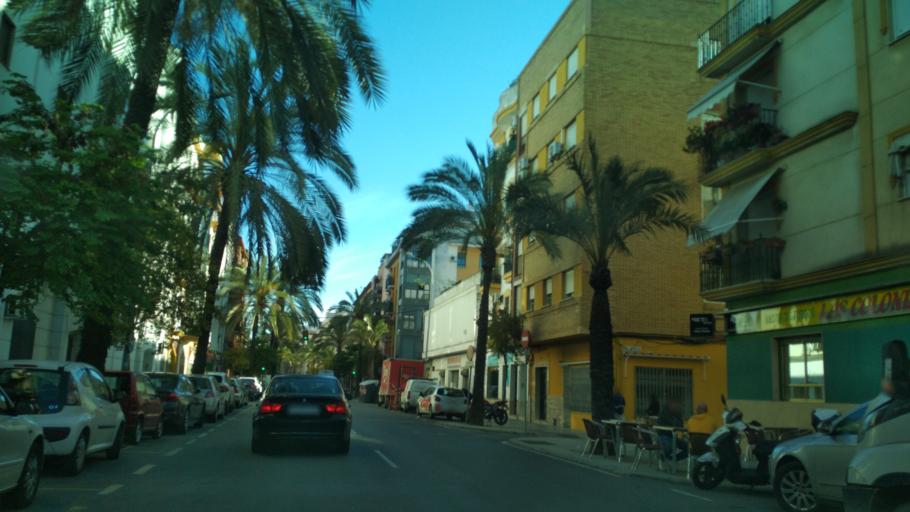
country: ES
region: Andalusia
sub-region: Provincia de Huelva
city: Huelva
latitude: 37.2699
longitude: -6.9509
